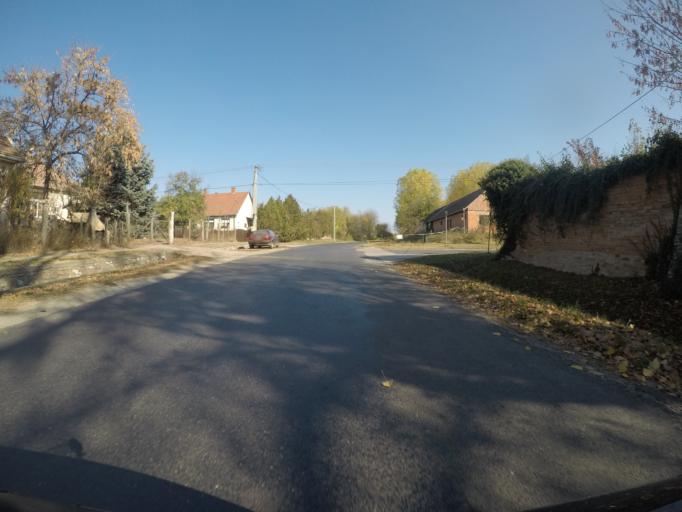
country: HU
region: Tolna
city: Nagydorog
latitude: 46.6298
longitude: 18.6578
